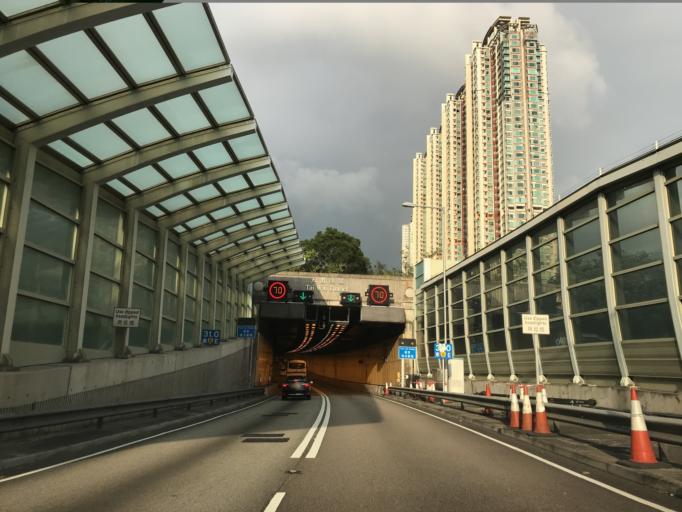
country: HK
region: Sha Tin
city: Sha Tin
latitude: 22.3675
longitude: 114.1715
